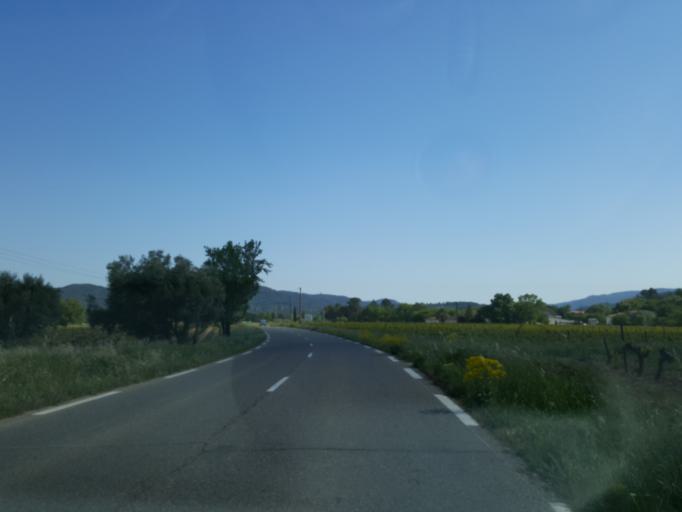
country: FR
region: Provence-Alpes-Cote d'Azur
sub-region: Departement du Var
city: La Roquebrussanne
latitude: 43.3327
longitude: 5.9806
